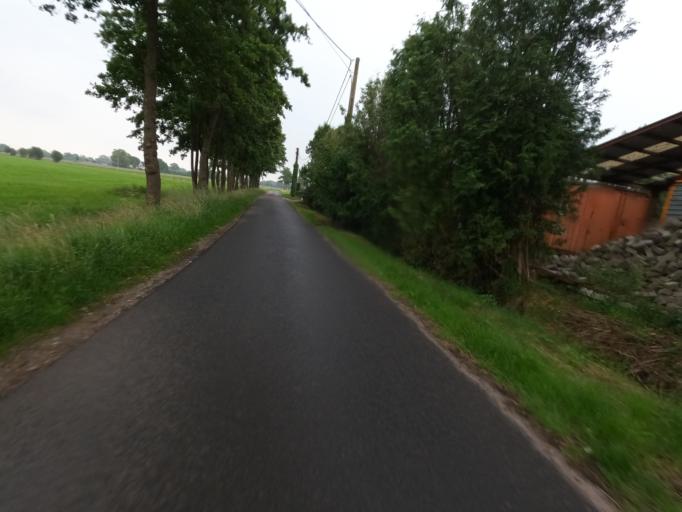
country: BE
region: Flanders
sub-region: Provincie Antwerpen
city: Kalmthout
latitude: 51.4280
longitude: 4.5160
